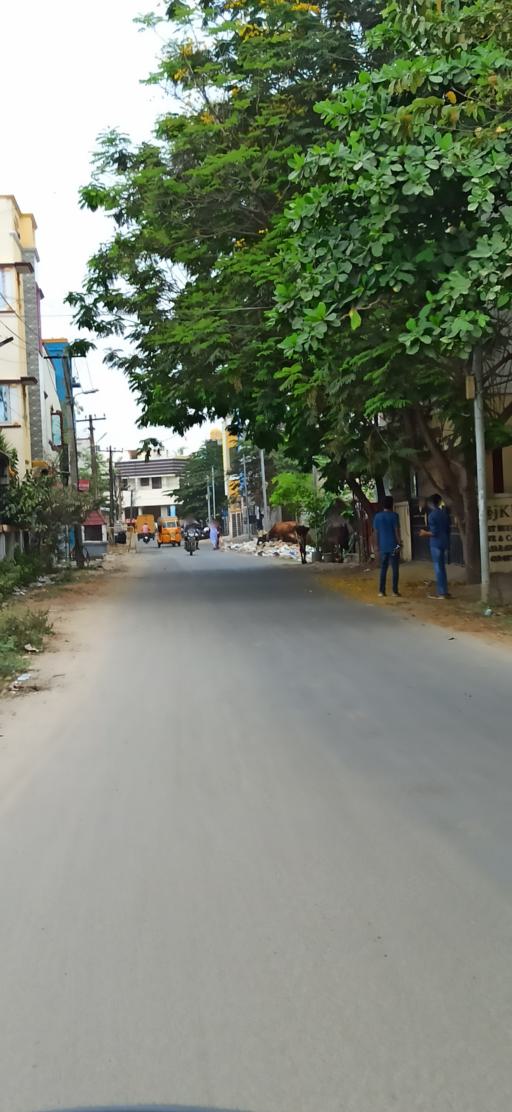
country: IN
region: Tamil Nadu
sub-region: Thiruvallur
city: Porur
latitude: 13.0182
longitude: 80.1455
